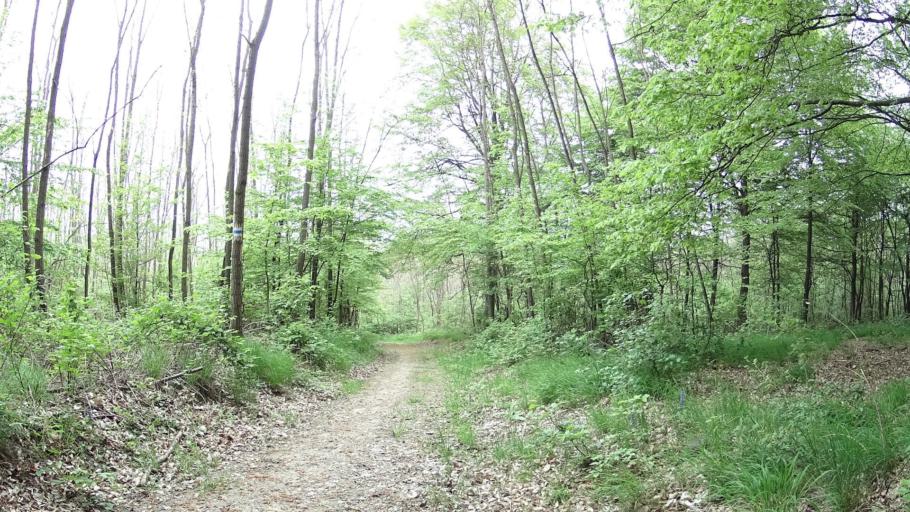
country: HU
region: Nograd
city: Romhany
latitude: 47.9041
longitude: 19.2445
